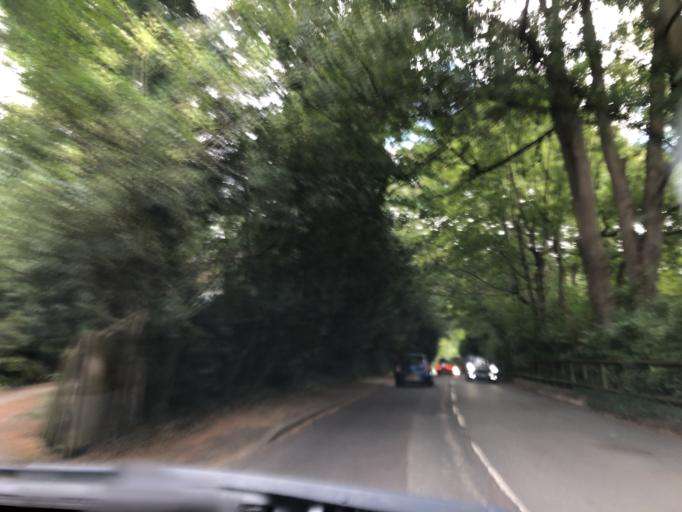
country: GB
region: England
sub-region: Kent
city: Westerham
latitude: 51.2621
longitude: 0.0784
